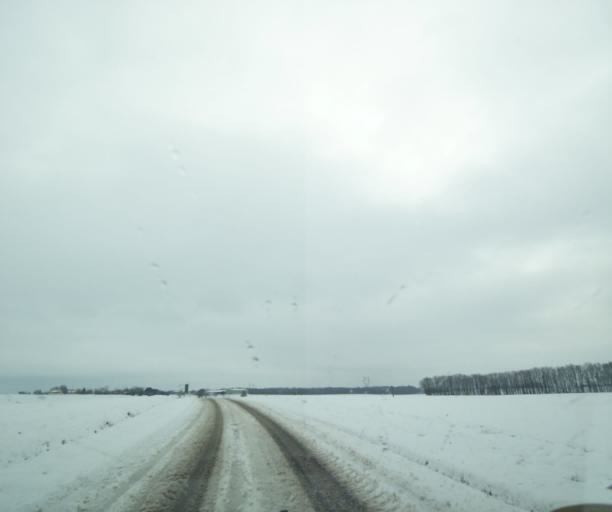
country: FR
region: Champagne-Ardenne
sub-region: Departement de la Haute-Marne
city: Montier-en-Der
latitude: 48.5154
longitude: 4.6815
